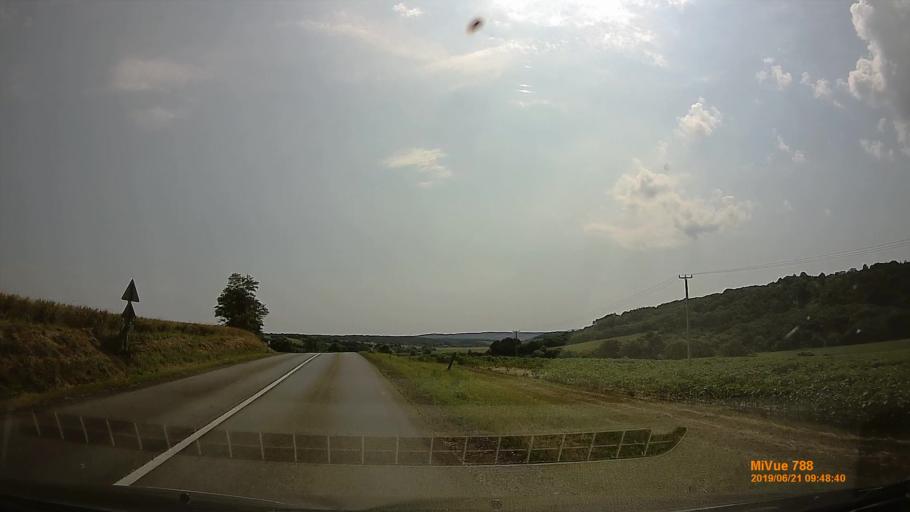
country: HU
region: Baranya
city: Sasd
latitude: 46.2678
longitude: 18.0325
